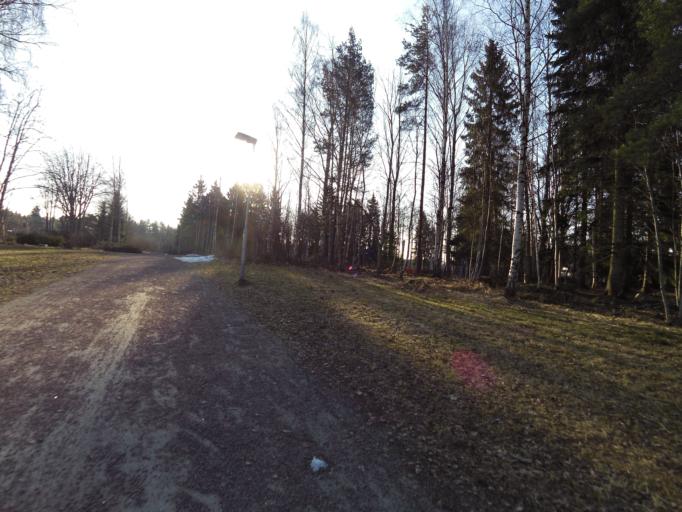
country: SE
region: Gaevleborg
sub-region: Gavle Kommun
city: Gavle
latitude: 60.6545
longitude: 17.1246
